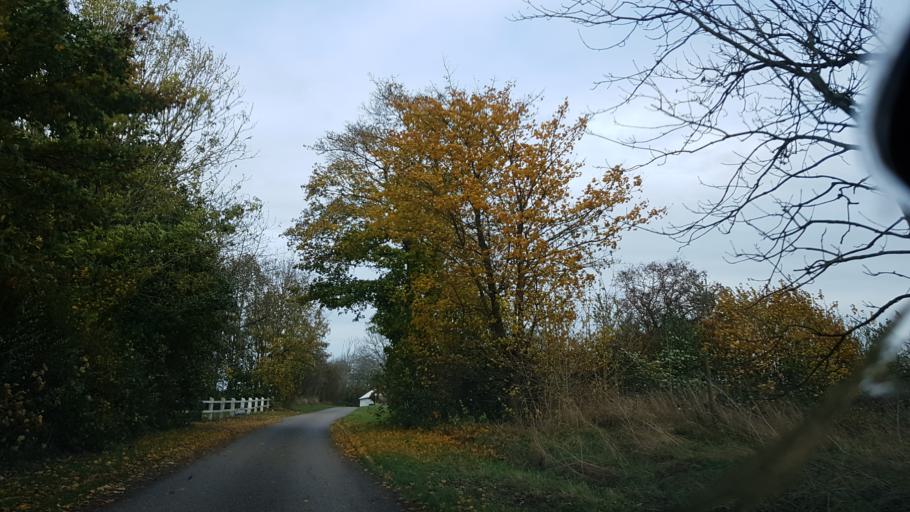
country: DK
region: South Denmark
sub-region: Haderslev Kommune
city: Vojens
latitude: 55.2517
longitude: 9.1906
